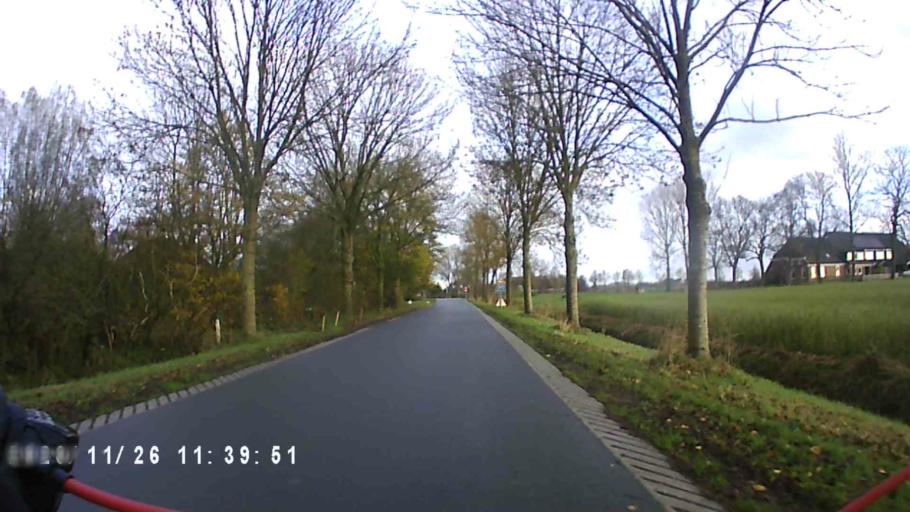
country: NL
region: Groningen
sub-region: Gemeente Bedum
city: Bedum
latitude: 53.2858
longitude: 6.5701
